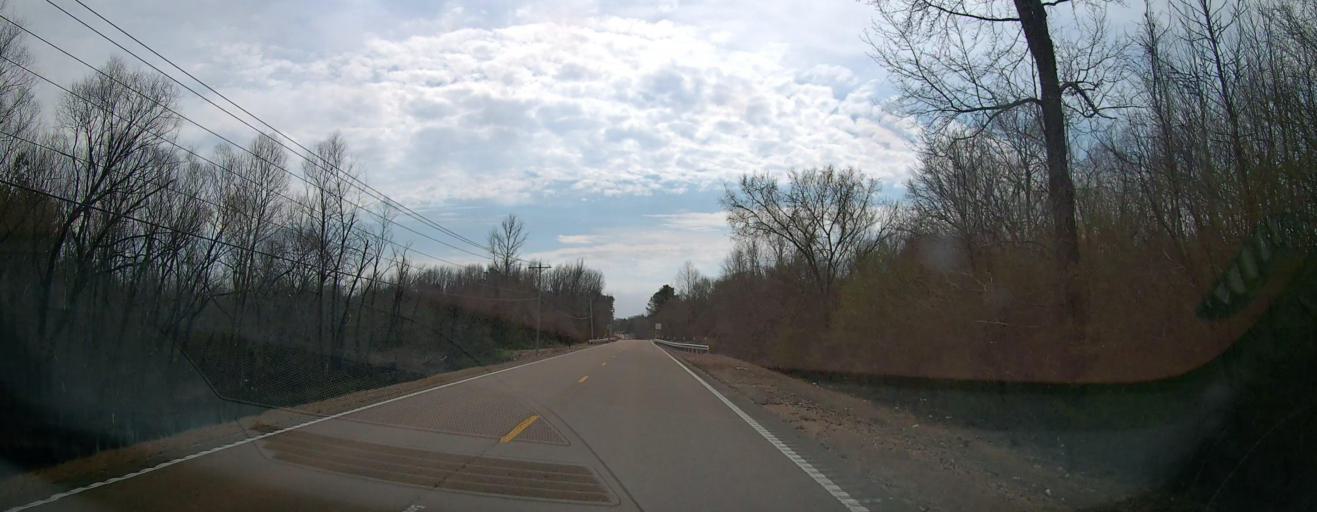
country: US
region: Mississippi
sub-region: Marshall County
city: Holly Springs
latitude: 34.7301
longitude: -89.4195
